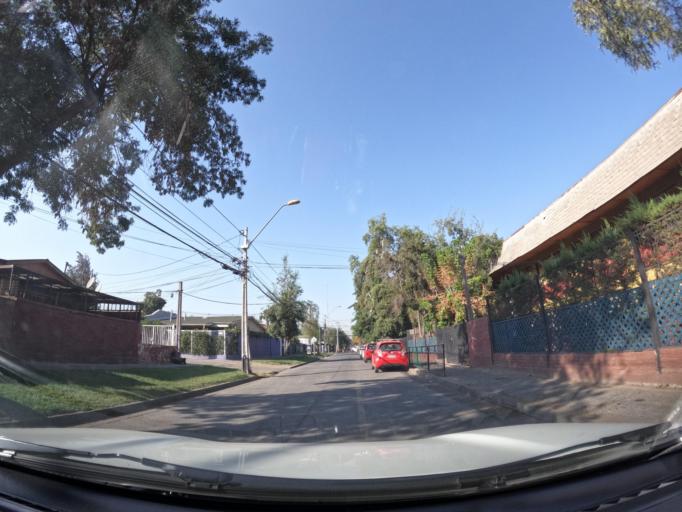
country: CL
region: Santiago Metropolitan
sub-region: Provincia de Santiago
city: Villa Presidente Frei, Nunoa, Santiago, Chile
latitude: -33.5074
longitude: -70.5640
